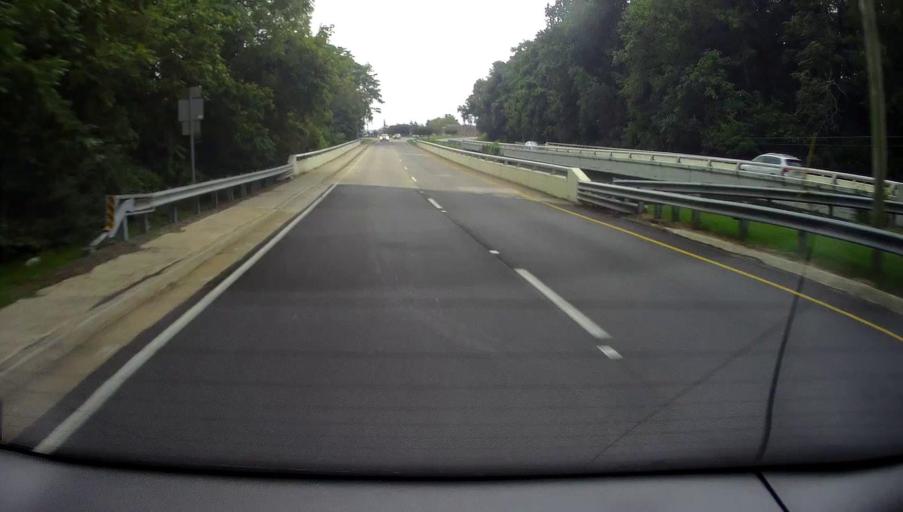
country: US
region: Tennessee
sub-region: Coffee County
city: Manchester
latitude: 35.4868
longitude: -86.0910
